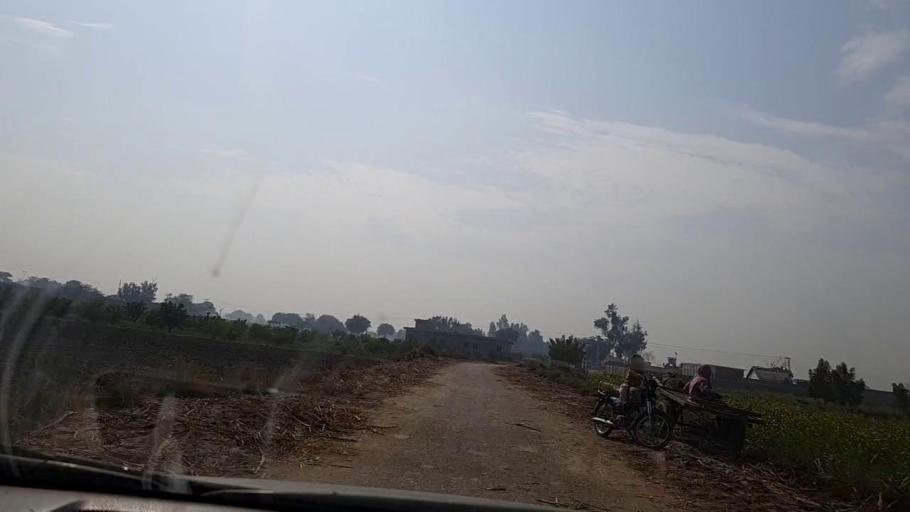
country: PK
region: Sindh
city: Daulatpur
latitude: 26.5342
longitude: 67.9863
